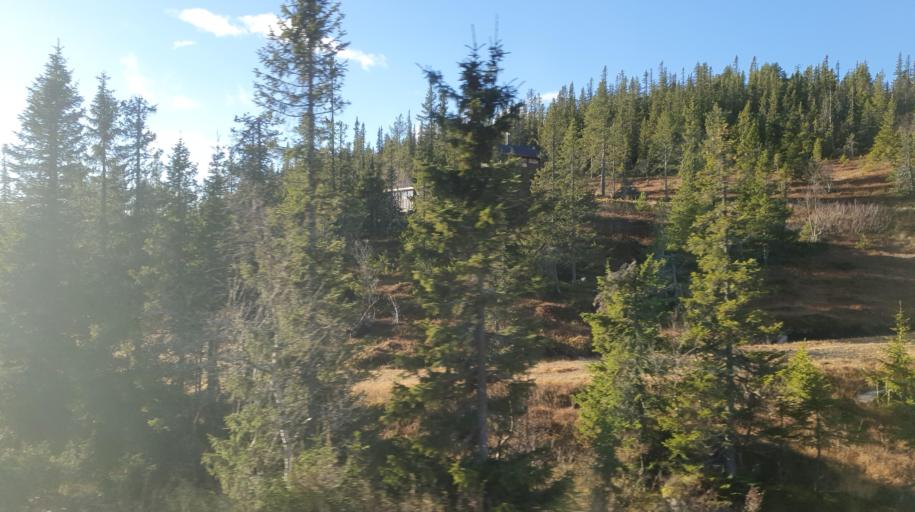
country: NO
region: Buskerud
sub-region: Krodsherad
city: Noresund
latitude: 60.2243
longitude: 9.5286
